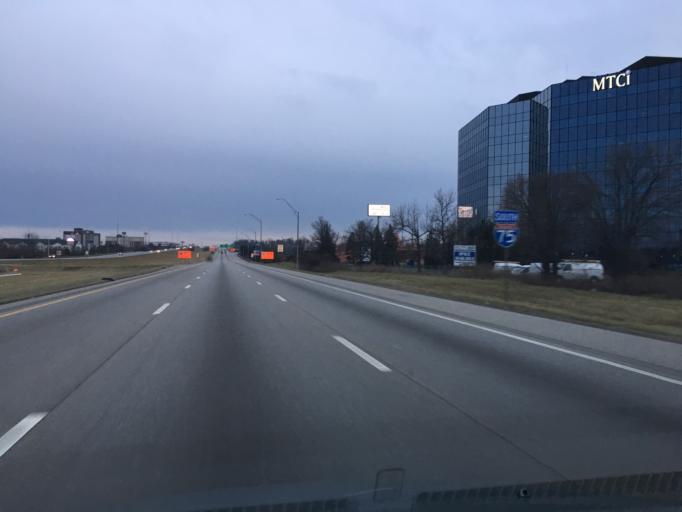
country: US
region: Ohio
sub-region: Hamilton County
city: Glendale
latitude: 39.2786
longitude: -84.4414
